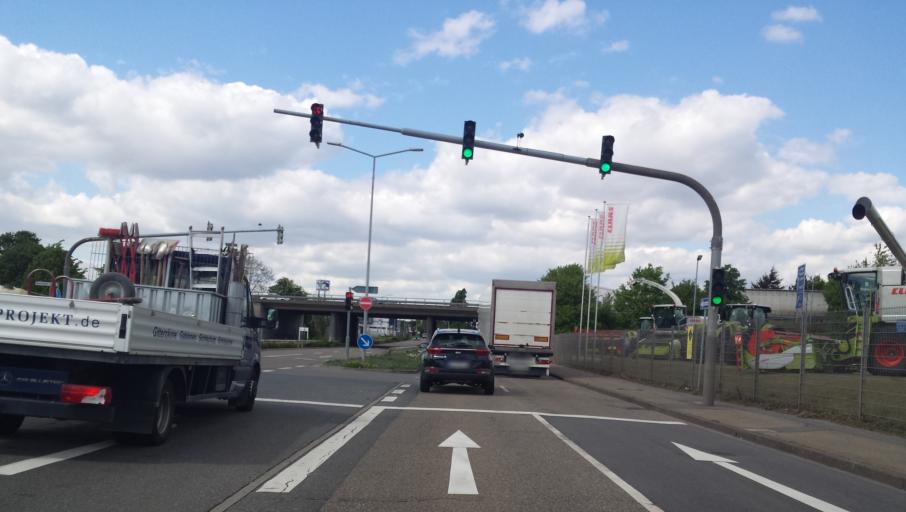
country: DE
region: Baden-Wuerttemberg
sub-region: Karlsruhe Region
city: Hockenheim
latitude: 49.3308
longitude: 8.5369
